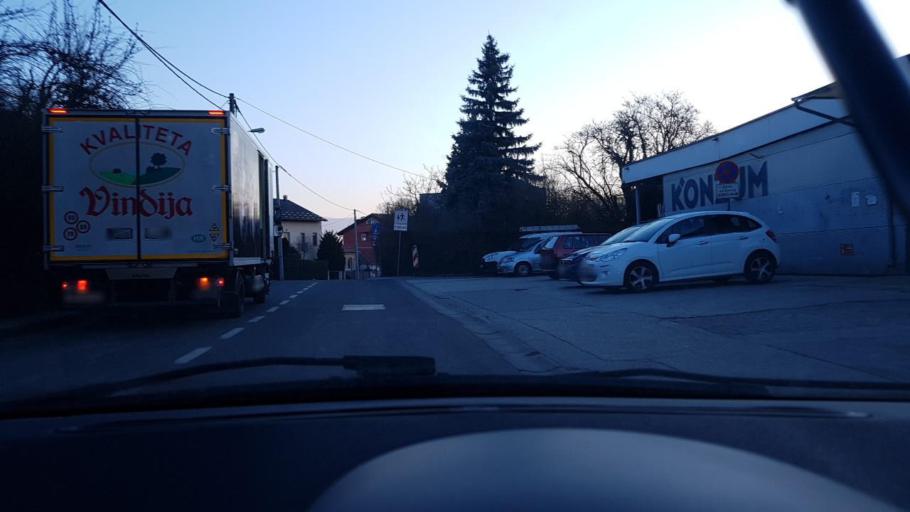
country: HR
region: Grad Zagreb
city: Zagreb
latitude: 45.8316
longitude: 15.9981
